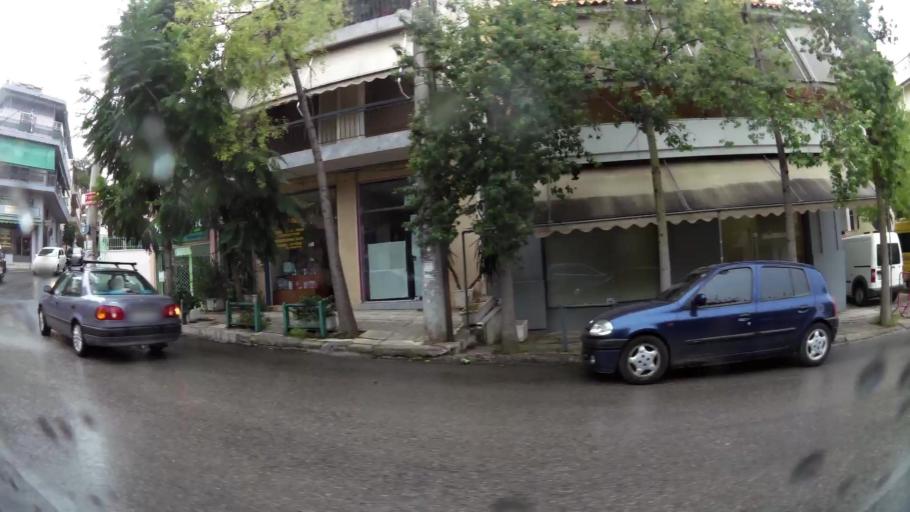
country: GR
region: Attica
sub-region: Nomarchia Athinas
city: Ymittos
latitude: 37.9525
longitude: 23.7522
